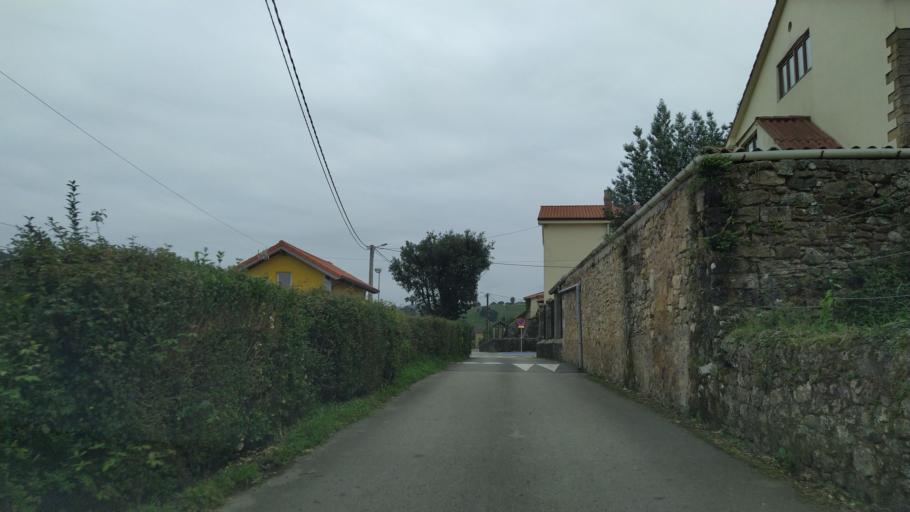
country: ES
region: Cantabria
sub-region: Provincia de Cantabria
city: Entrambasaguas
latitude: 43.3766
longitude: -3.7186
